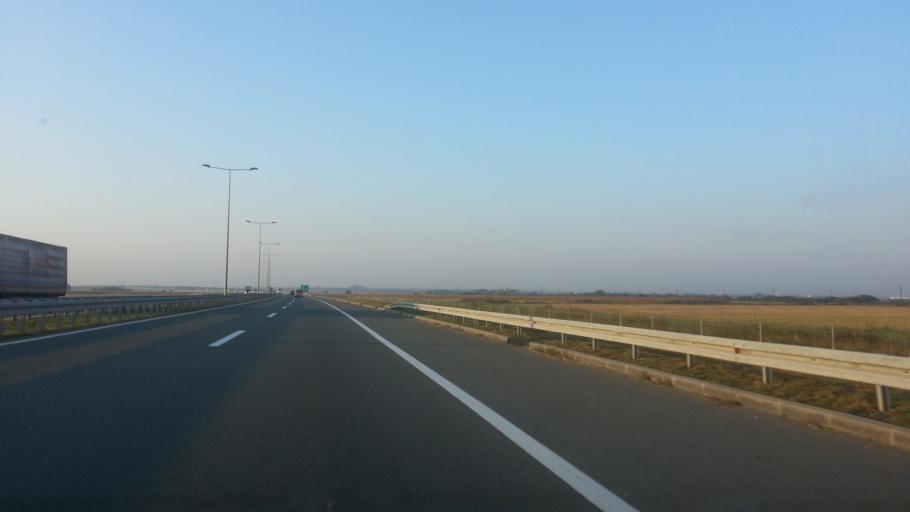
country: RS
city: Dobanovci
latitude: 44.8594
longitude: 20.2502
